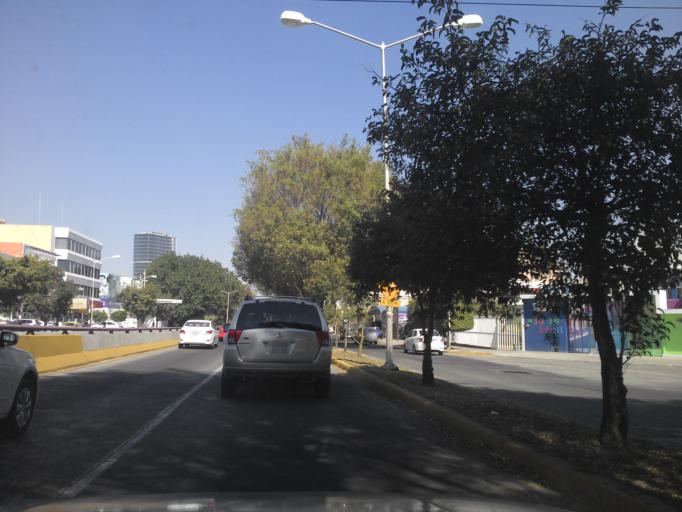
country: MX
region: Jalisco
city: Guadalajara
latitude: 20.6911
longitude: -103.3763
